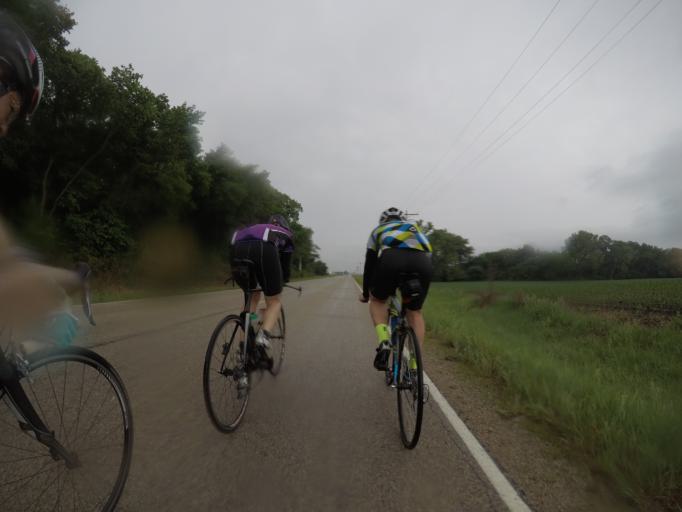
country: US
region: Kansas
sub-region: Pottawatomie County
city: Wamego
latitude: 39.3348
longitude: -96.2213
